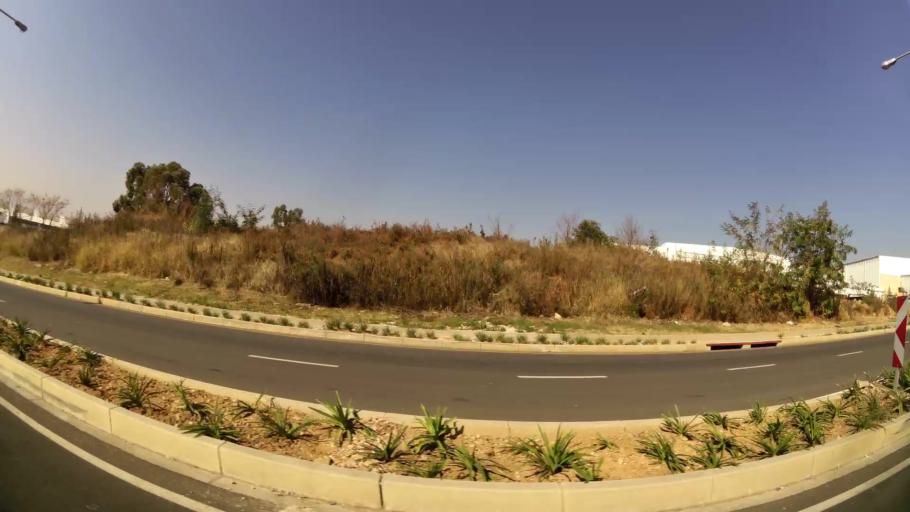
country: ZA
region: Gauteng
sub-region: City of Johannesburg Metropolitan Municipality
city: Modderfontein
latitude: -26.1000
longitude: 28.1374
